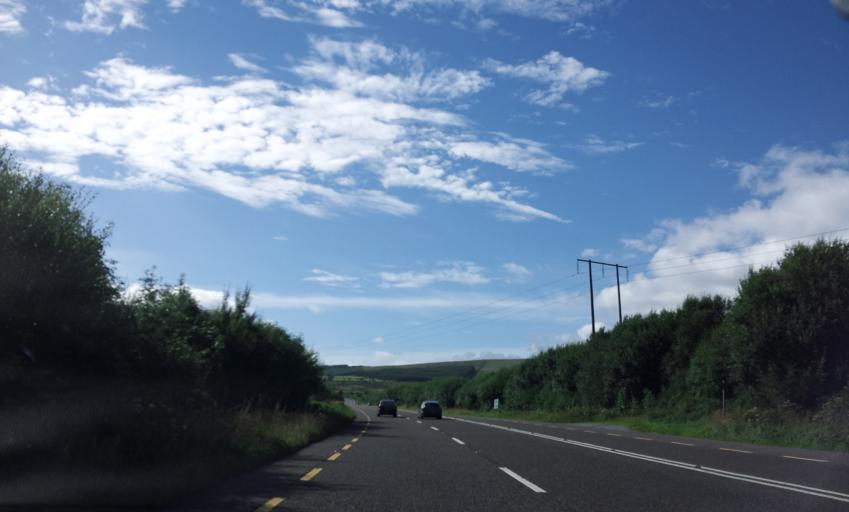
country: IE
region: Munster
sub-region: County Cork
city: Millstreet
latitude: 51.9578
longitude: -9.1926
